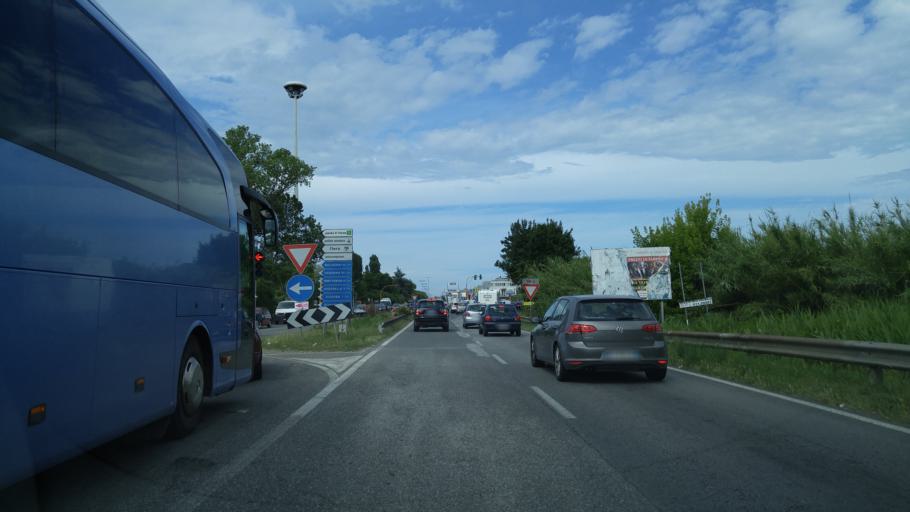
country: IT
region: Emilia-Romagna
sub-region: Provincia di Rimini
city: Rimini
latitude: 44.0412
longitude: 12.5701
